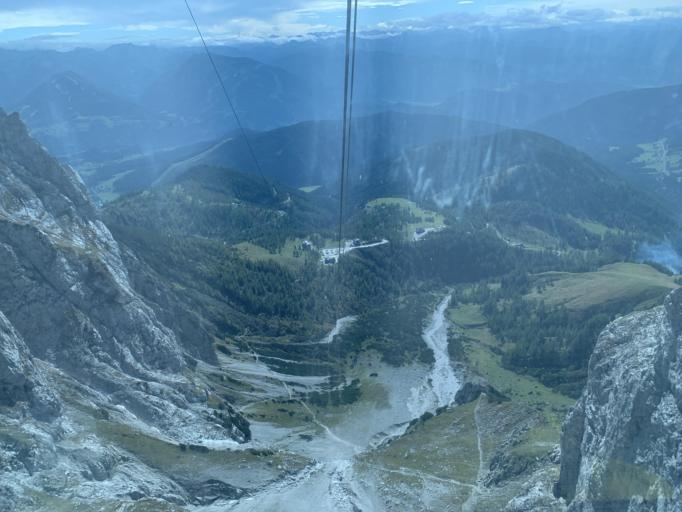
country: AT
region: Styria
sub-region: Politischer Bezirk Liezen
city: Schladming
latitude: 47.4628
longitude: 13.6238
